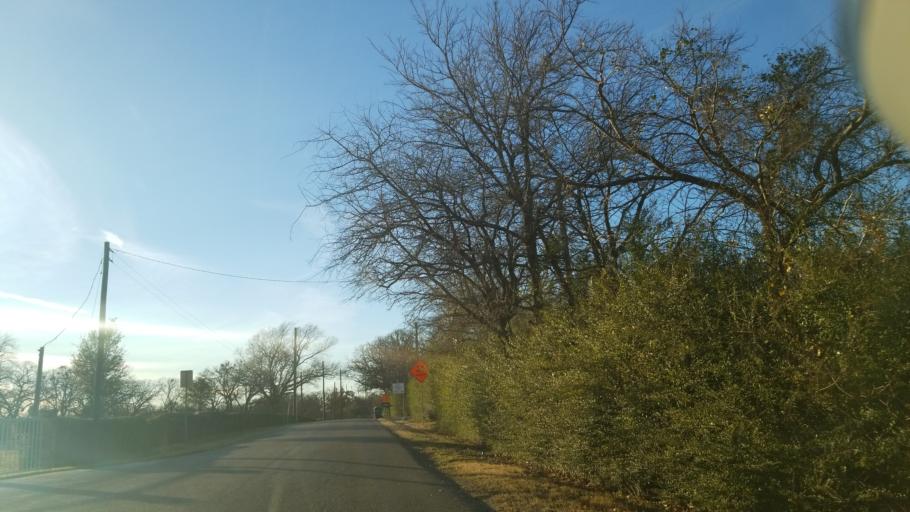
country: US
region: Texas
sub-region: Denton County
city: Denton
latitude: 33.1835
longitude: -97.1571
